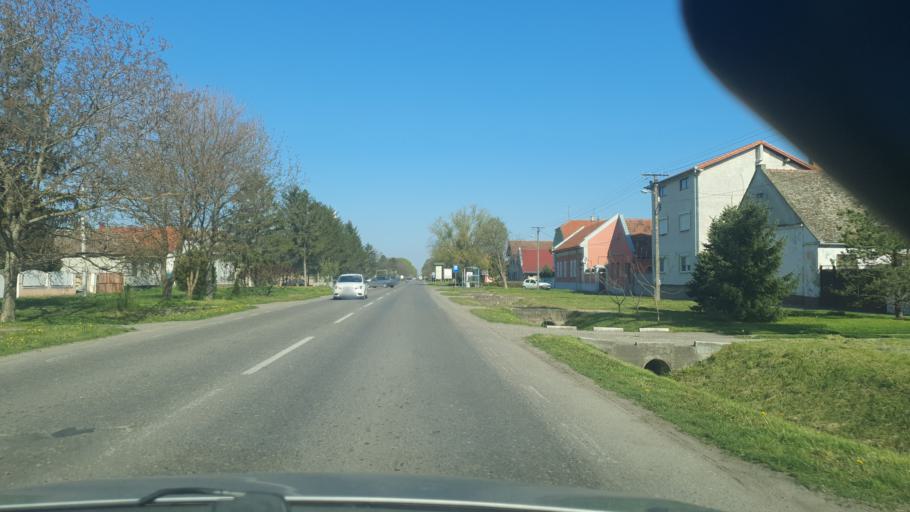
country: RS
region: Autonomna Pokrajina Vojvodina
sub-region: Zapadnobacki Okrug
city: Kula
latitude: 45.6545
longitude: 19.4645
